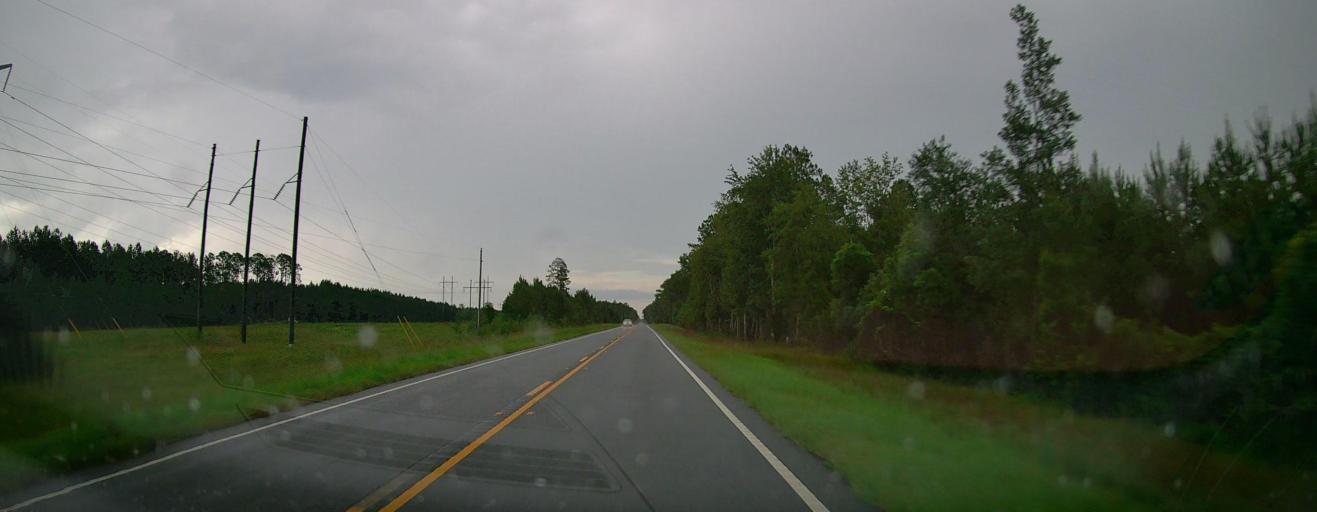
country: US
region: Georgia
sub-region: Brantley County
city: Nahunta
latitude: 31.3399
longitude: -81.8438
